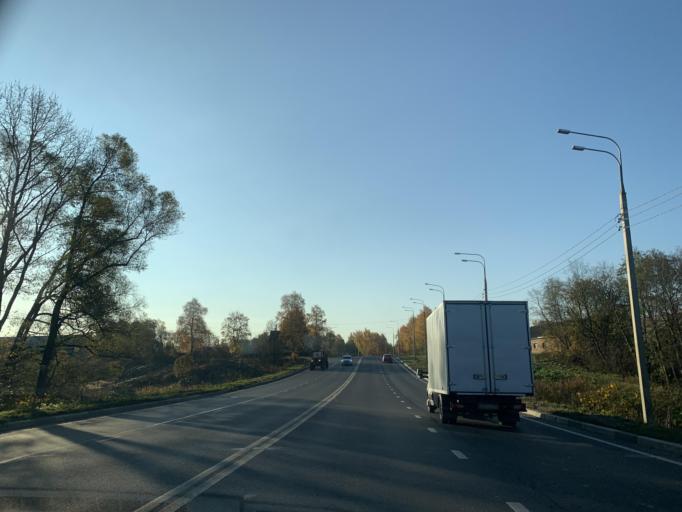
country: RU
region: Jaroslavl
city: Konstantinovskiy
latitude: 57.7622
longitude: 39.6844
